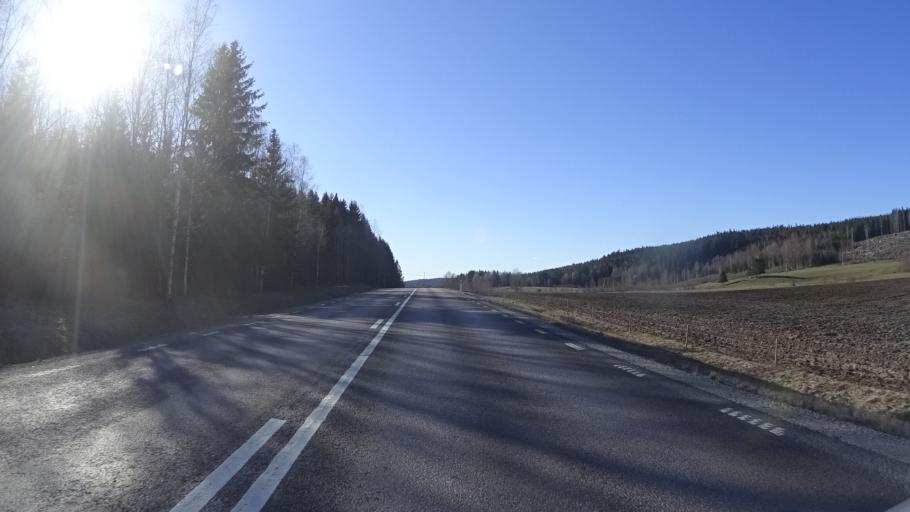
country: SE
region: Vaermland
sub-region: Arvika Kommun
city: Arvika
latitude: 59.6682
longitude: 12.8268
